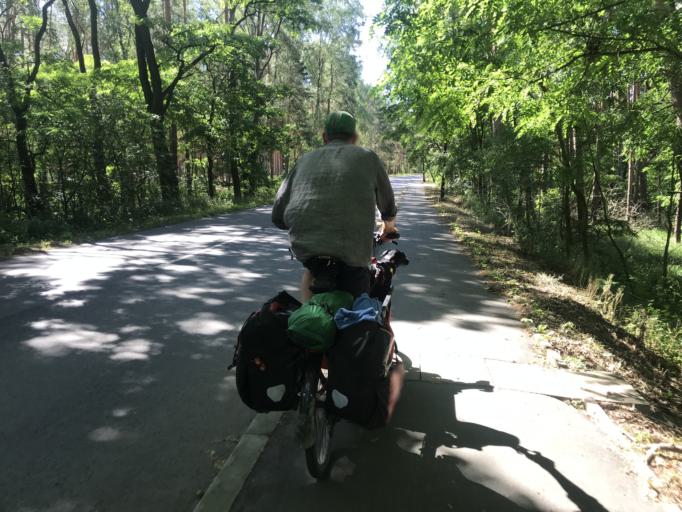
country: PL
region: Lubusz
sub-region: Powiat krosnienski
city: Gubin
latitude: 52.0398
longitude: 14.7644
